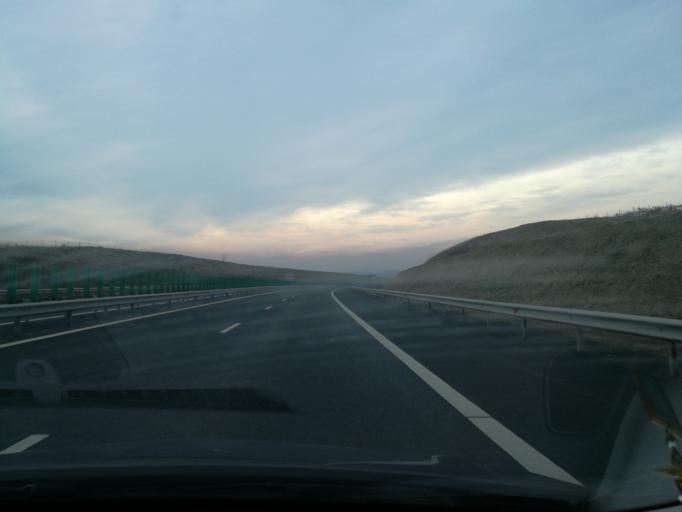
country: RO
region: Constanta
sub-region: Oras Cernavoda
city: Cernavoda
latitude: 44.3123
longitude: 28.0366
